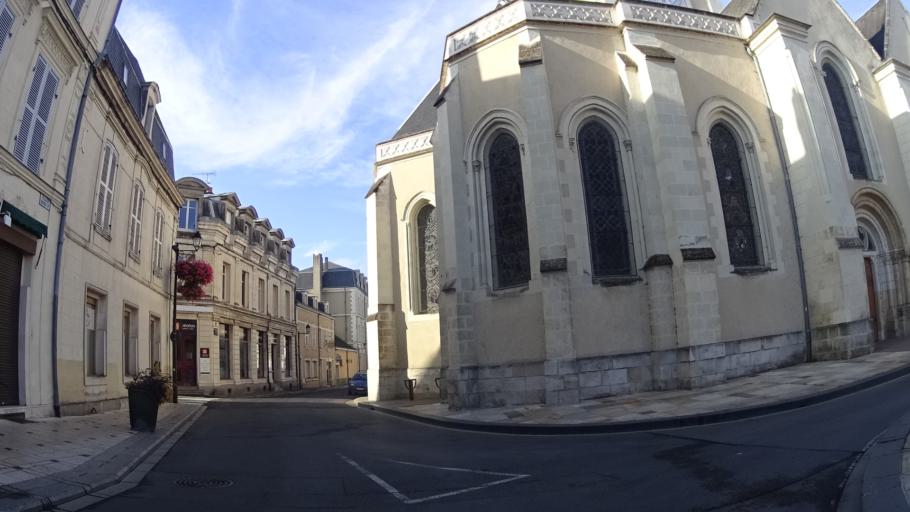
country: FR
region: Pays de la Loire
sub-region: Departement de la Sarthe
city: La Fleche
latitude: 47.6992
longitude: -0.0750
